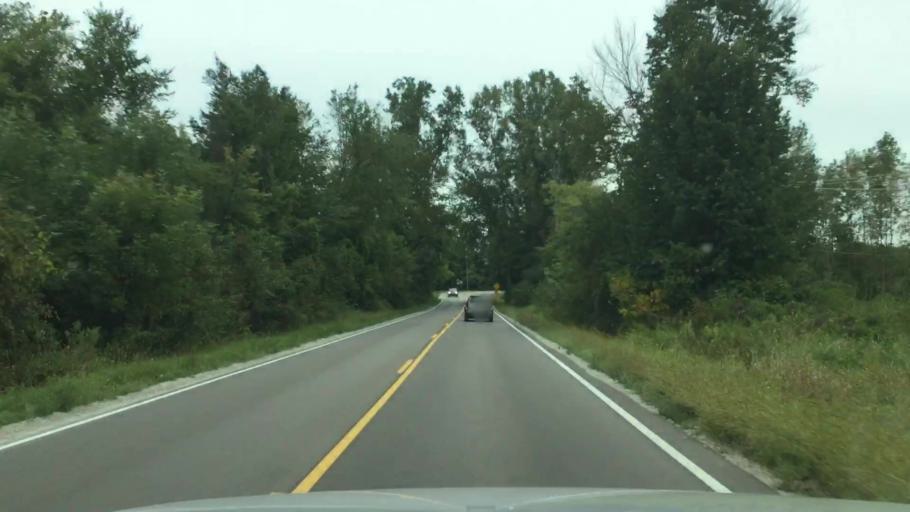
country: US
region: Michigan
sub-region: Washtenaw County
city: Ypsilanti
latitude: 42.2071
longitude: -83.6210
